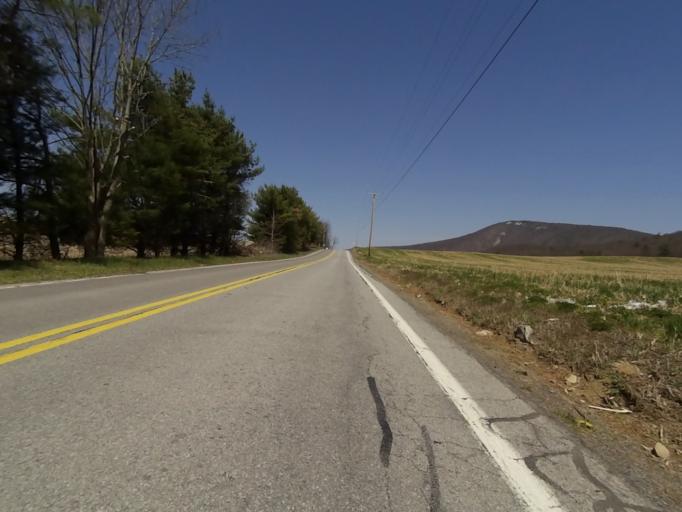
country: US
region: Pennsylvania
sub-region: Blair County
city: Tyrone
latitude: 40.5907
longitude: -78.1380
